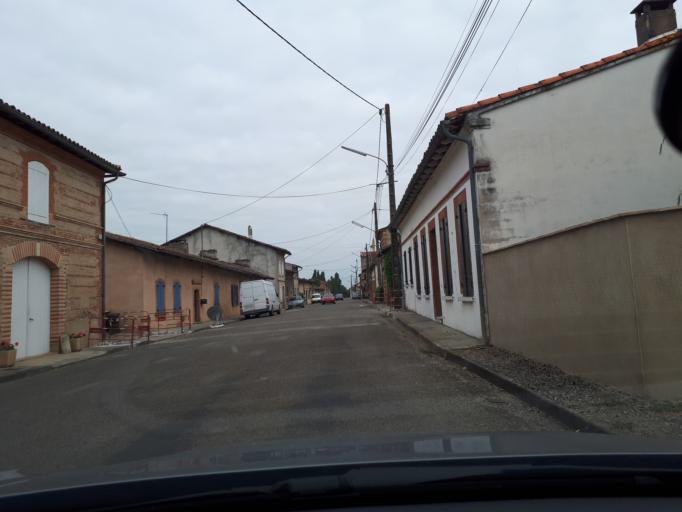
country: FR
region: Midi-Pyrenees
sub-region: Departement de la Haute-Garonne
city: Fronton
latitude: 43.8593
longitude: 1.3508
